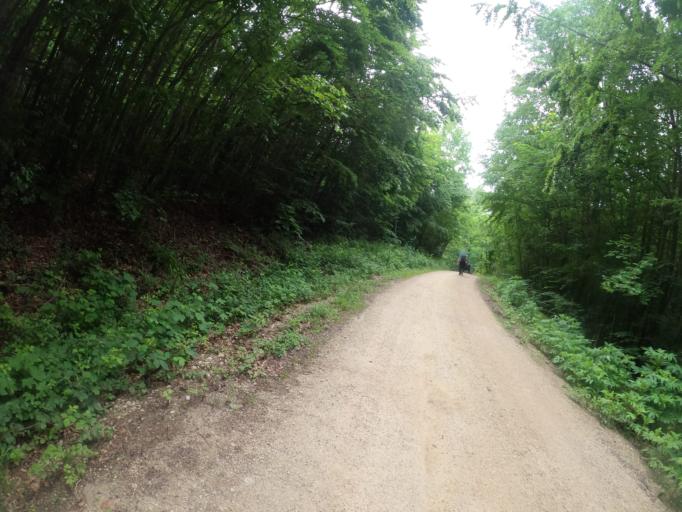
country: DE
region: Bavaria
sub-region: Upper Franconia
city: Litzendorf
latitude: 49.9250
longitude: 11.0339
